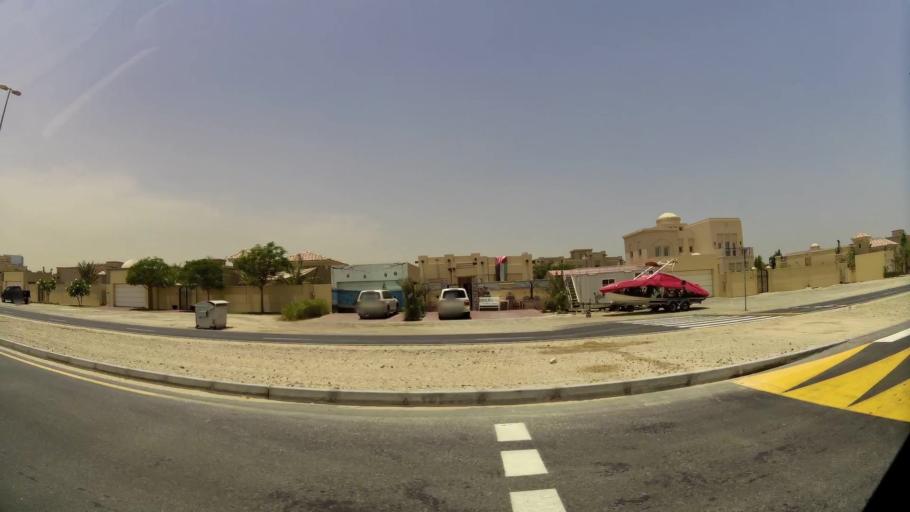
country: AE
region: Dubai
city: Dubai
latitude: 25.0863
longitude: 55.2385
